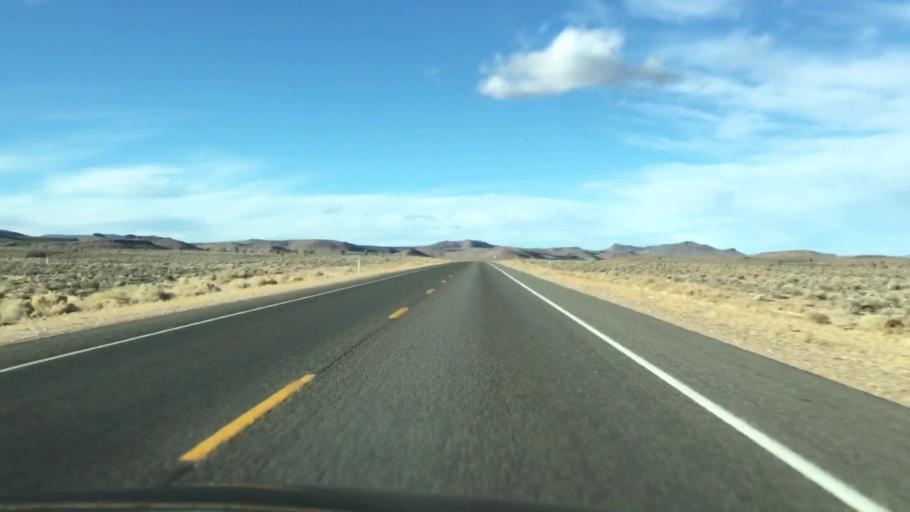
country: US
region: Nevada
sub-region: Esmeralda County
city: Goldfield
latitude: 37.5950
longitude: -117.2105
